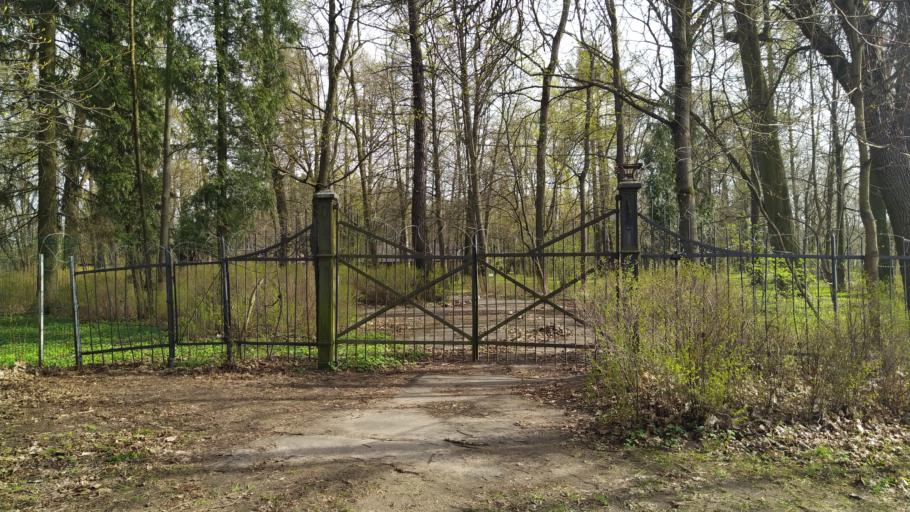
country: RU
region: St.-Petersburg
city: Pushkin
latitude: 59.7136
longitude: 30.4223
